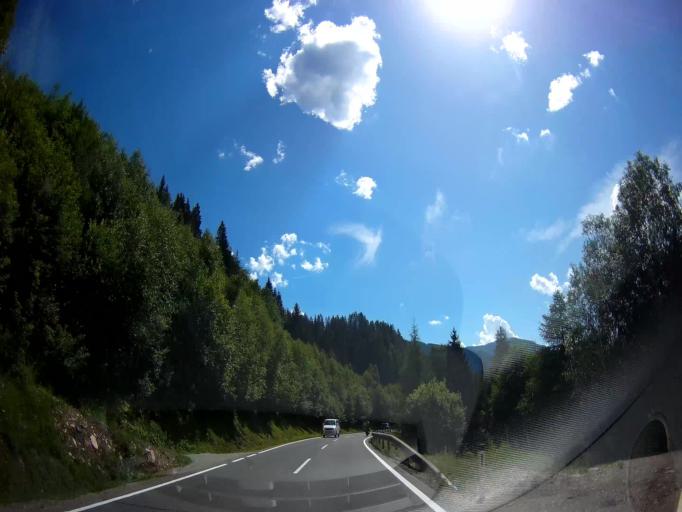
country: AT
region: Styria
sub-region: Politischer Bezirk Murau
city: Stadl an der Mur
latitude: 47.0759
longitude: 13.9232
